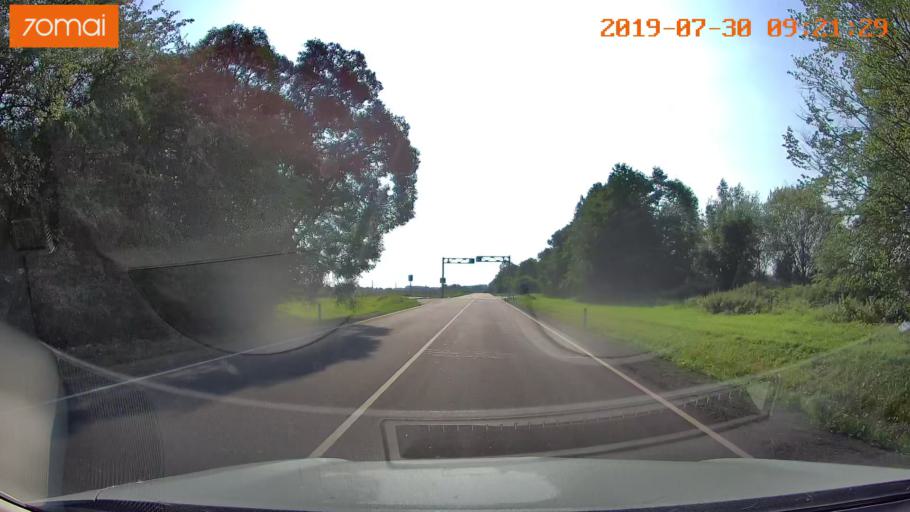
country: RU
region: Kaliningrad
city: Nesterov
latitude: 54.6354
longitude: 22.6325
